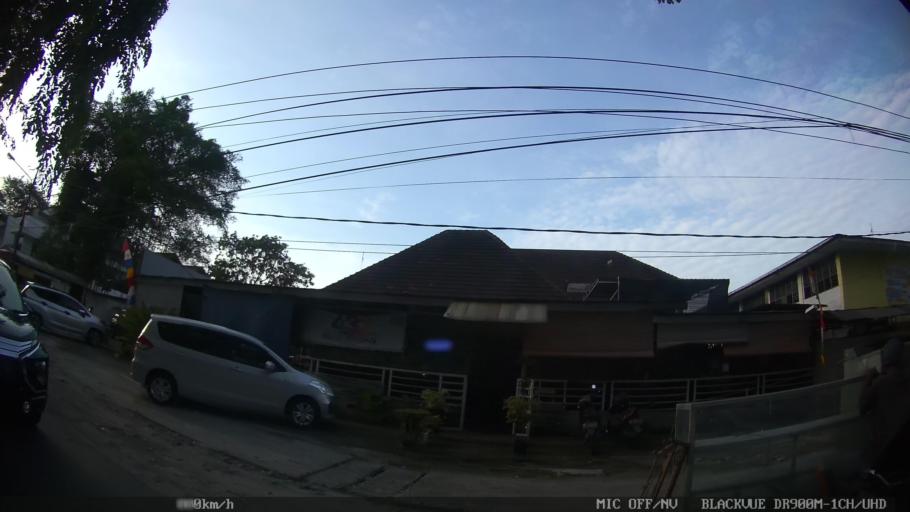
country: ID
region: North Sumatra
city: Medan
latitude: 3.5766
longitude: 98.6657
